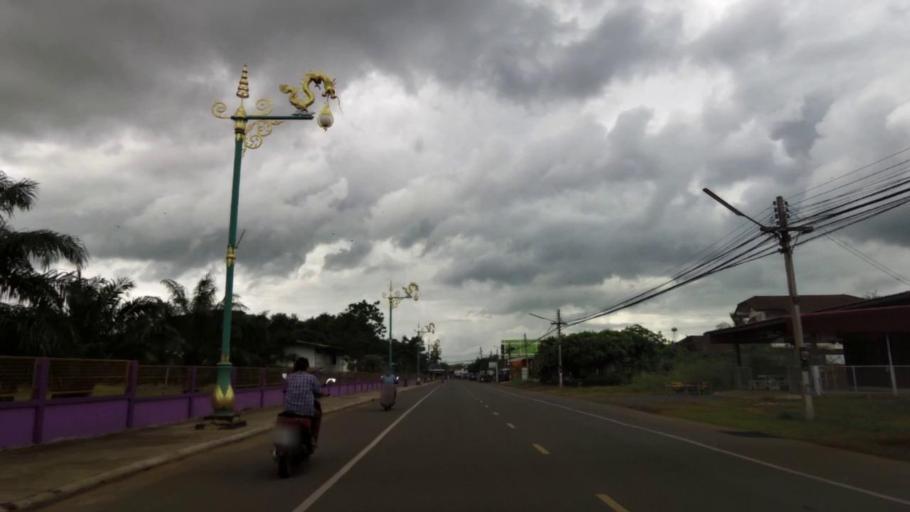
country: TH
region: Nakhon Sawan
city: Phai Sali
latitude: 15.5996
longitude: 100.6555
